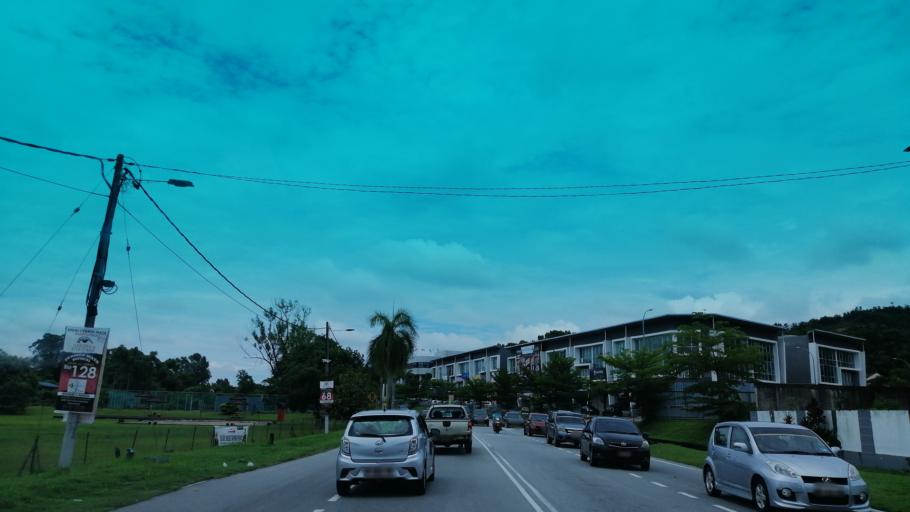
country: MY
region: Perak
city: Taiping
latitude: 4.8599
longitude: 100.7375
